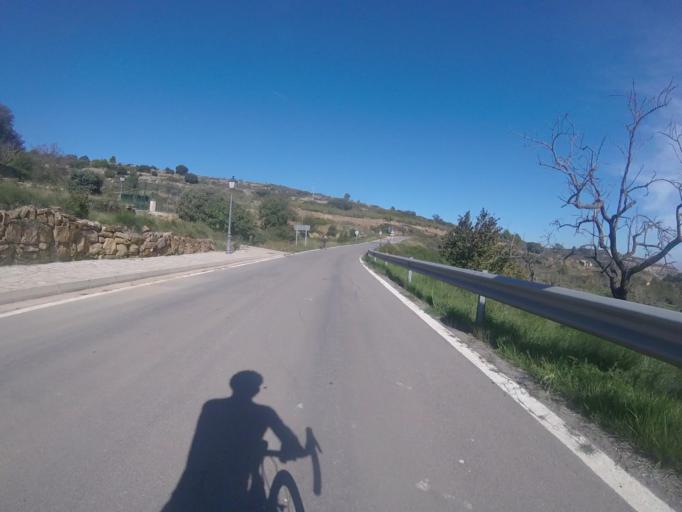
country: ES
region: Valencia
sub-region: Provincia de Castello
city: Sarratella
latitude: 40.3145
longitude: 0.0298
